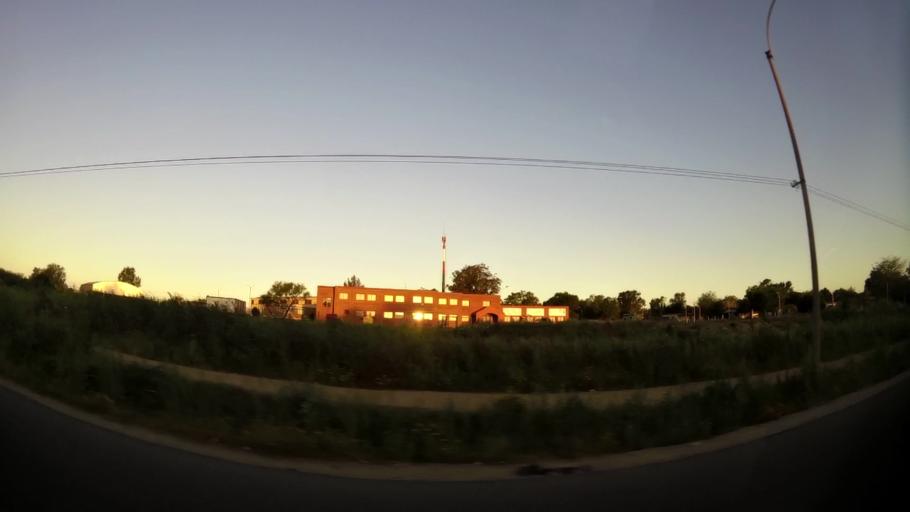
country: UY
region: Canelones
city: La Paz
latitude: -34.8231
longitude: -56.1689
